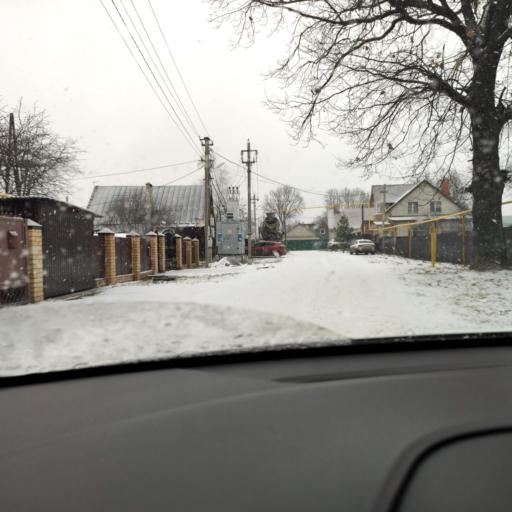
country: RU
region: Tatarstan
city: Osinovo
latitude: 55.8623
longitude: 48.9151
